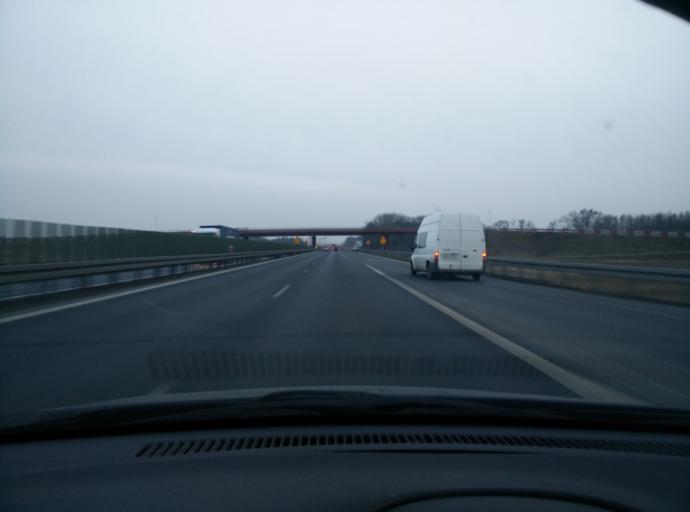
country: PL
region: Greater Poland Voivodeship
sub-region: Powiat poznanski
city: Daszewice
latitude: 52.3244
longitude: 17.0319
